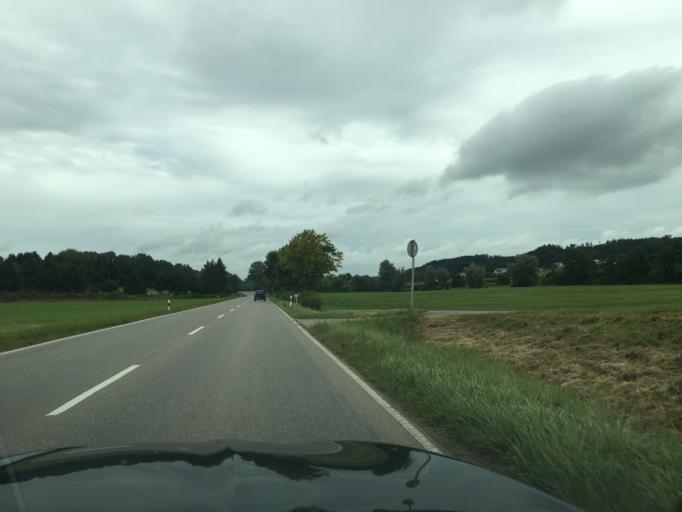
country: DE
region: Bavaria
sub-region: Swabia
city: Altenmunster
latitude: 48.4525
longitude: 10.5878
